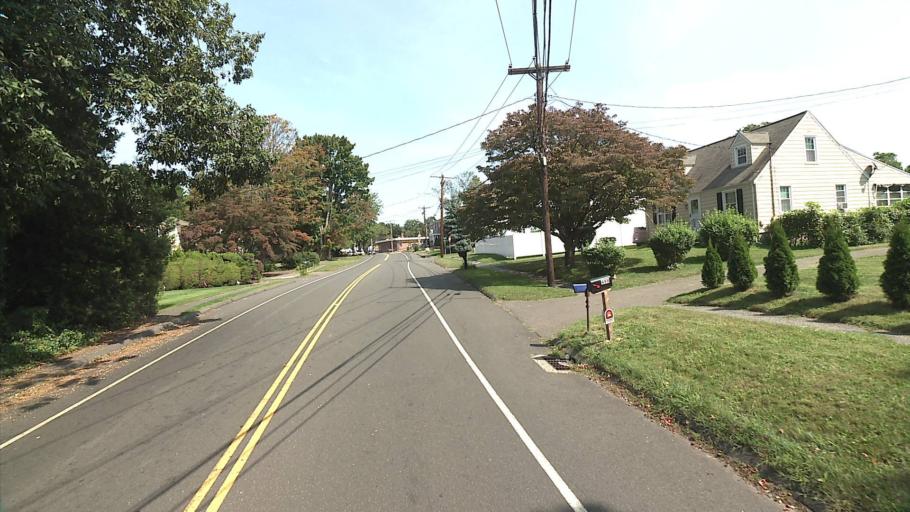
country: US
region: Connecticut
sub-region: Fairfield County
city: Fairfield
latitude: 41.1797
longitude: -73.2528
